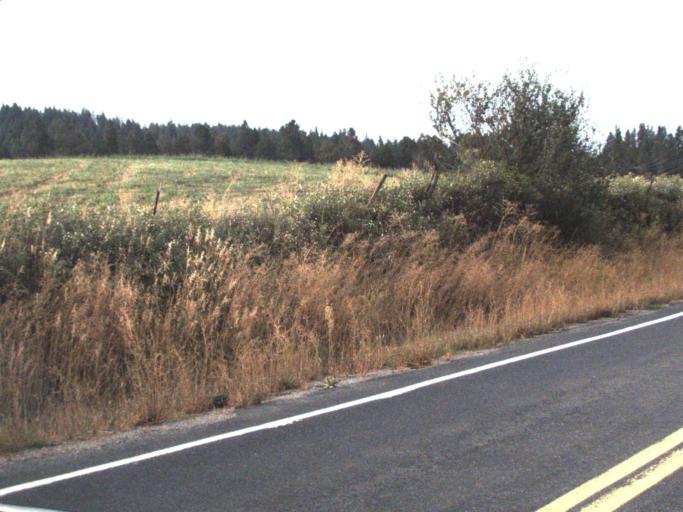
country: US
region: Washington
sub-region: Stevens County
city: Chewelah
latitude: 48.1052
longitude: -117.7574
